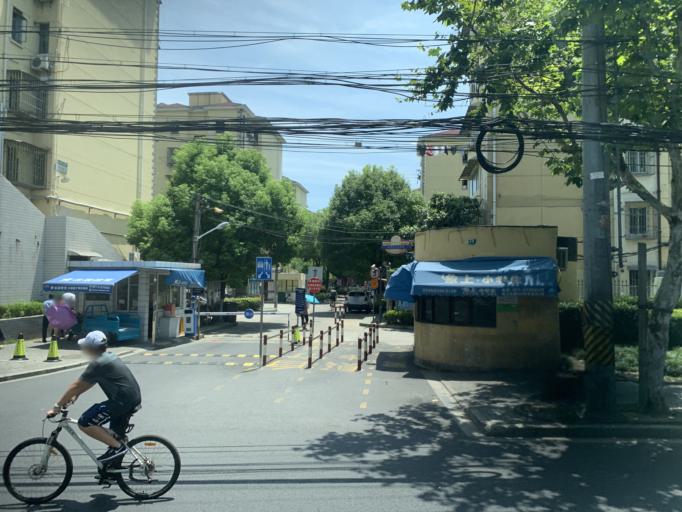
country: CN
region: Shanghai Shi
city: Pudong
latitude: 31.2507
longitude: 121.5754
